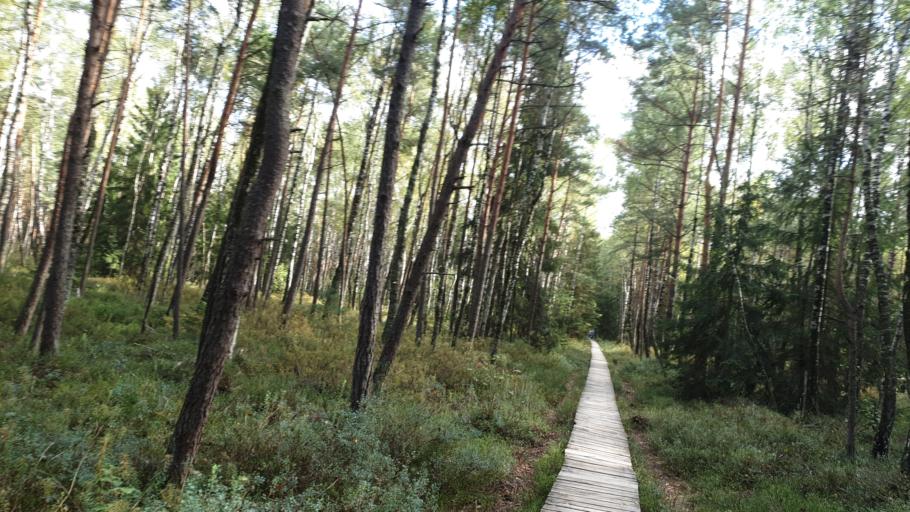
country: LT
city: Trakai
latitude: 54.6406
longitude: 24.9687
